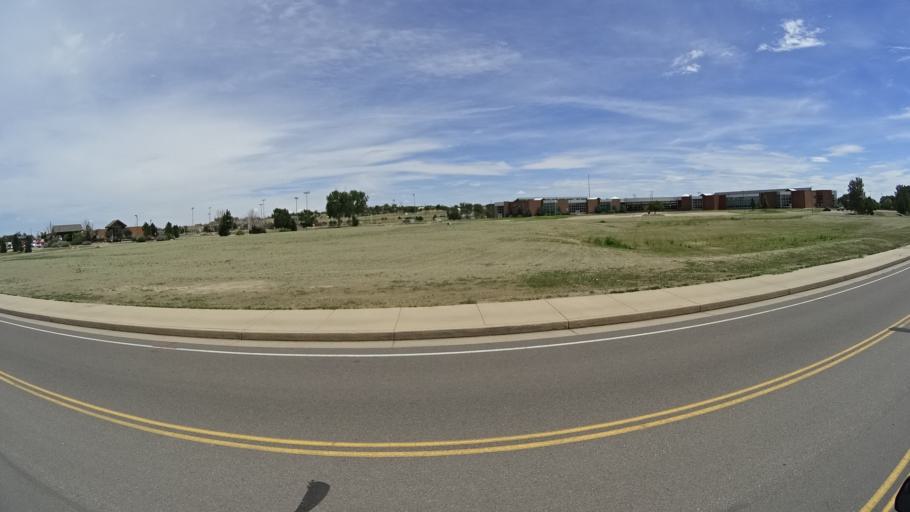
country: US
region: Colorado
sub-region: El Paso County
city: Fountain
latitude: 38.6738
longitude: -104.6870
